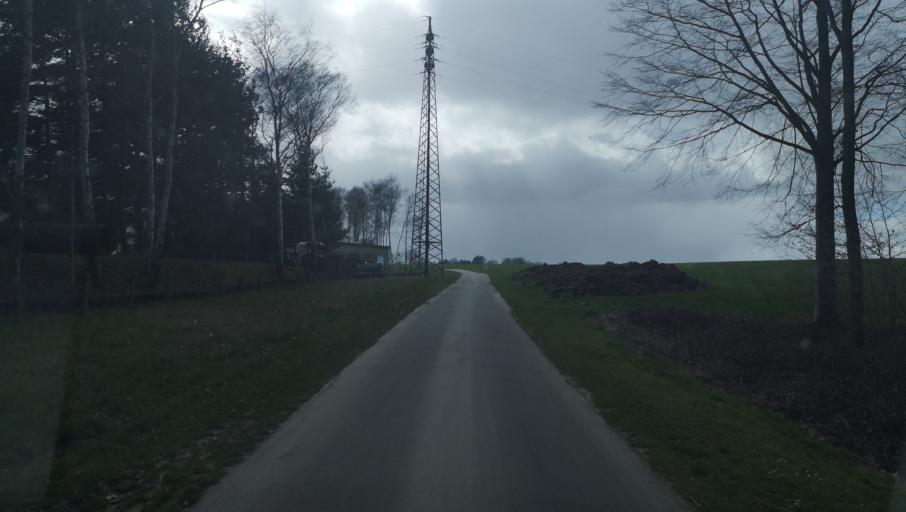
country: BE
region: Wallonia
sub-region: Province de Namur
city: Namur
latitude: 50.5005
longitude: 4.8593
